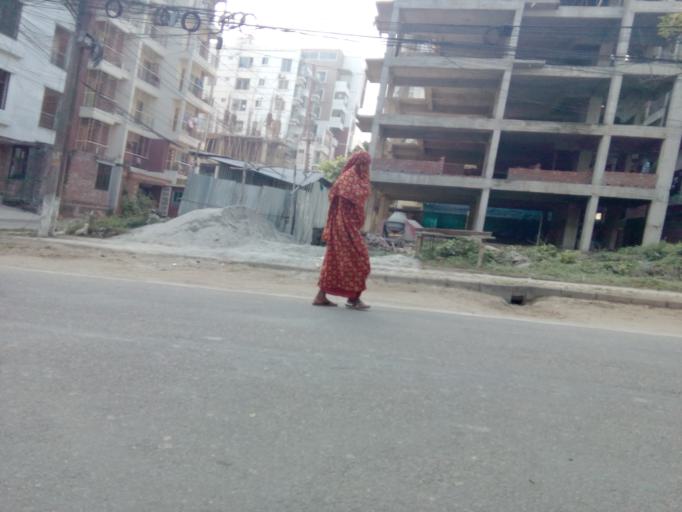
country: BD
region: Dhaka
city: Tungi
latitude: 23.8159
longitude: 90.4342
